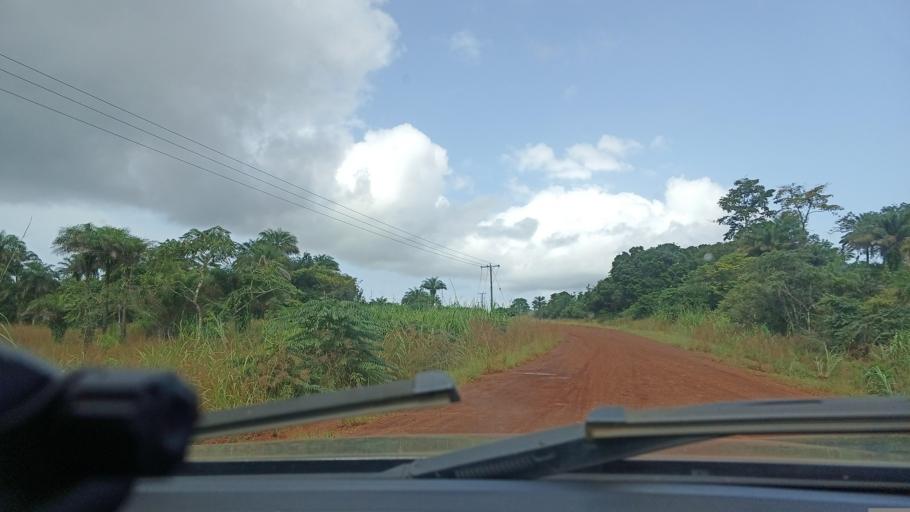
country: LR
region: Grand Cape Mount
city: Robertsport
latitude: 6.6910
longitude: -11.2632
